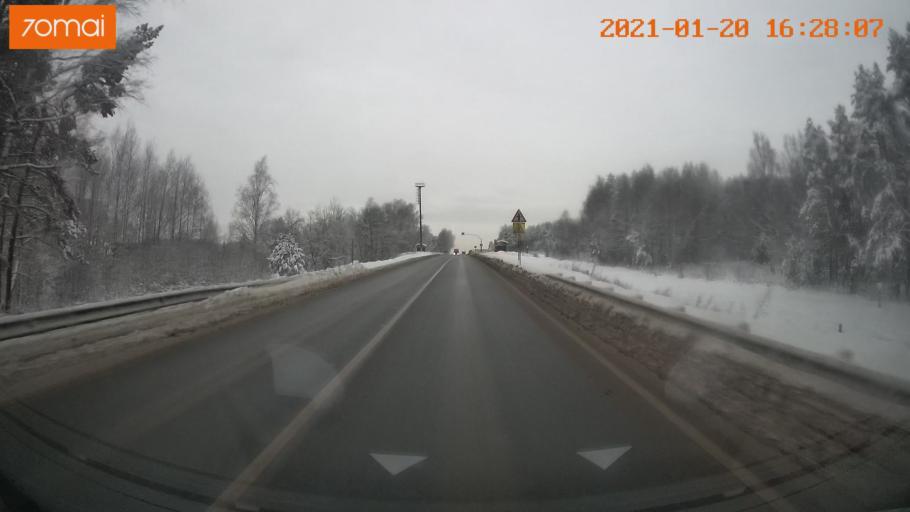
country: RU
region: Vladimir
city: Kameshkovo
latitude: 56.1940
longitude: 40.9241
